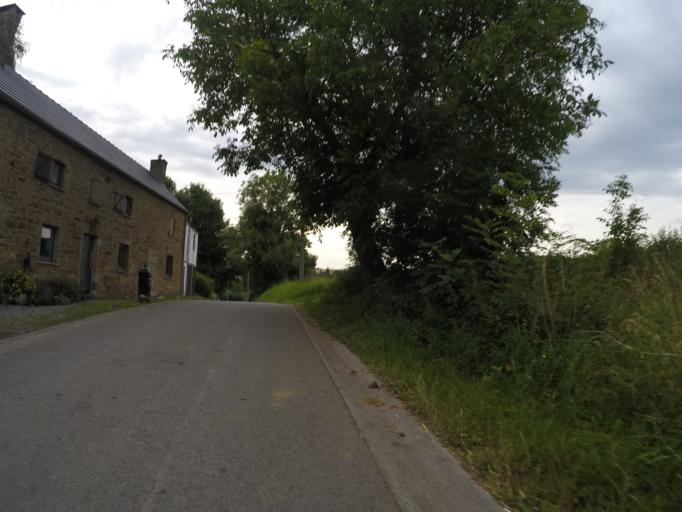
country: BE
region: Wallonia
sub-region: Province de Namur
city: Assesse
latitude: 50.3304
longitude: 5.0356
